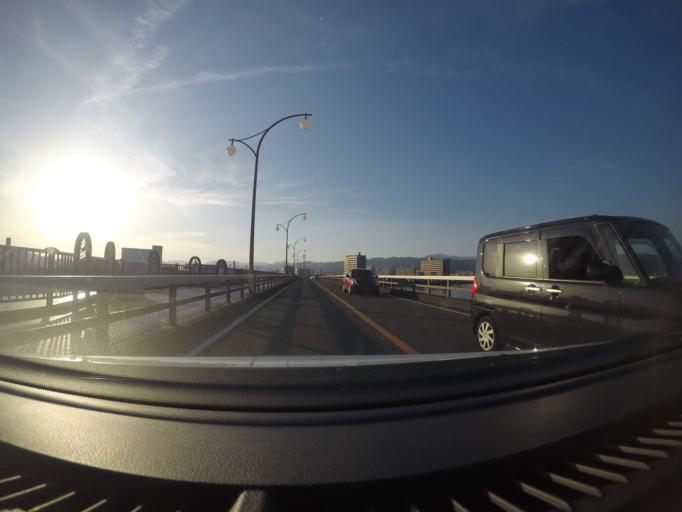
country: JP
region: Kochi
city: Kochi-shi
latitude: 33.5497
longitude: 133.5671
